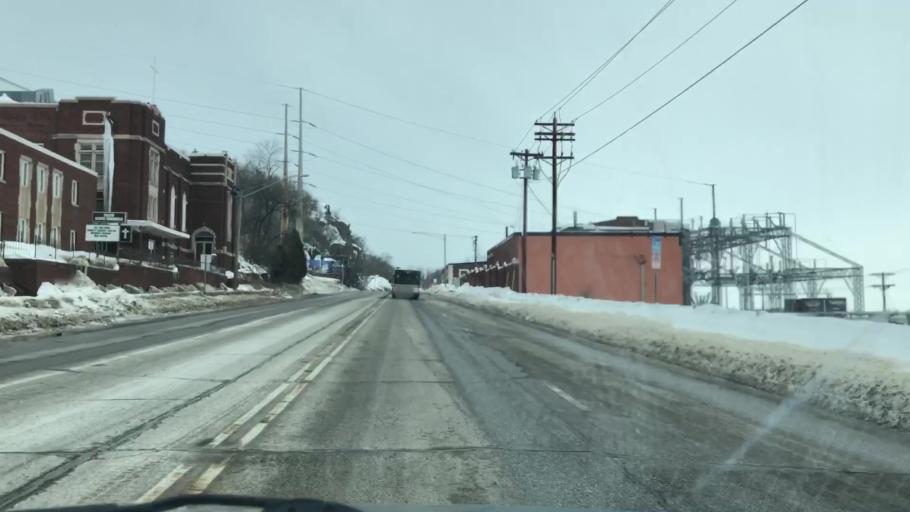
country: US
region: Minnesota
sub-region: Saint Louis County
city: Duluth
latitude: 46.7718
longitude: -92.1180
